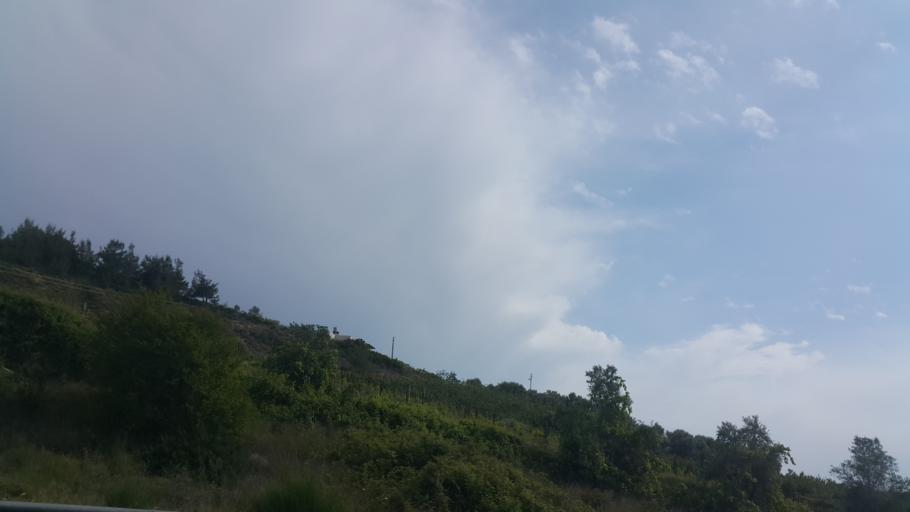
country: TR
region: Mersin
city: Tarsus
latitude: 36.9524
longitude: 34.8313
